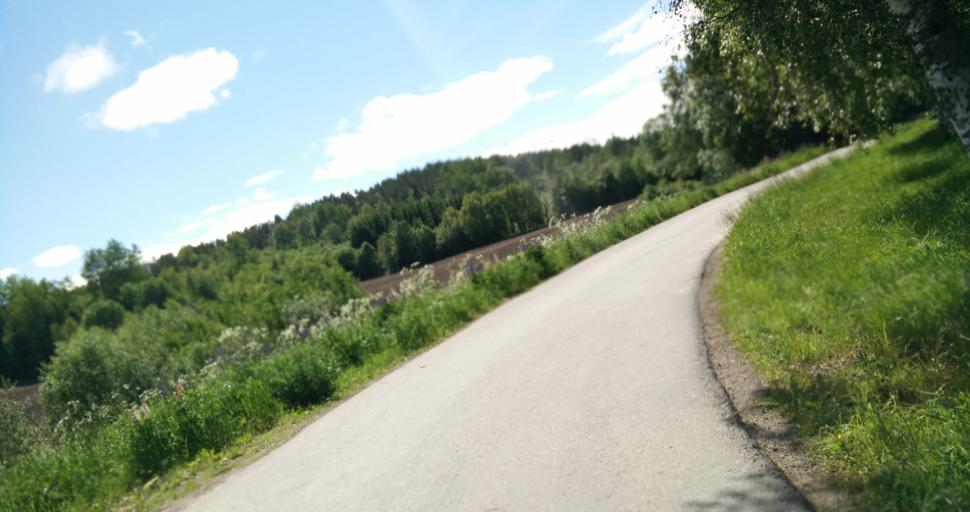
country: SE
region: Vaesternorrland
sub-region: Sundsvalls Kommun
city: Nolby
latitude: 62.2856
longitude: 17.3679
